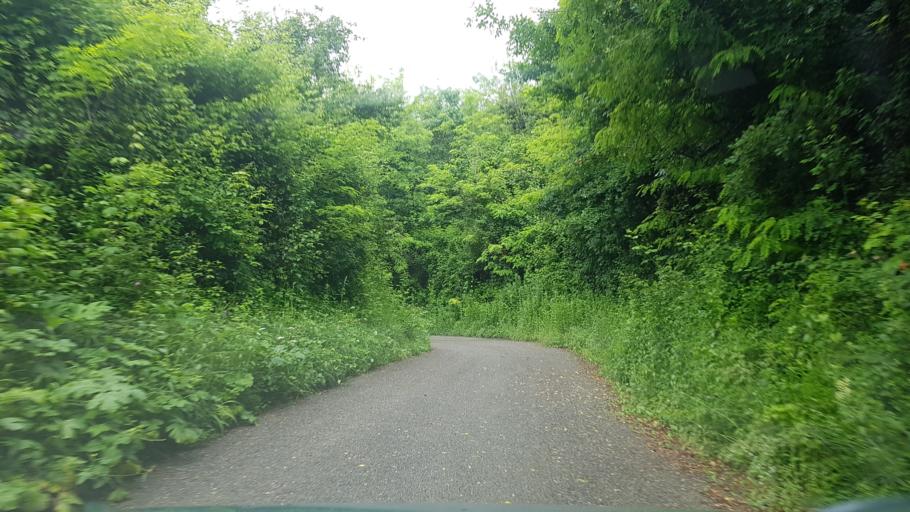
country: IT
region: Friuli Venezia Giulia
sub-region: Provincia di Gorizia
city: San Floriano del Collio
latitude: 45.9499
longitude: 13.5849
